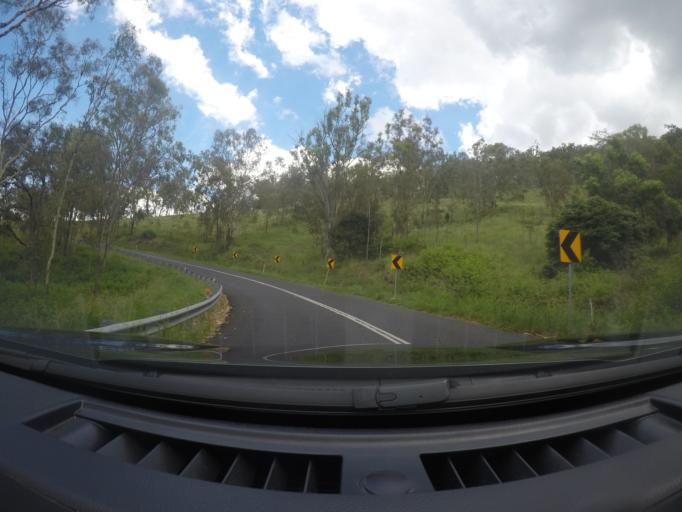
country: AU
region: Queensland
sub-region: Moreton Bay
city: Woodford
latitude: -27.0717
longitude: 152.5617
